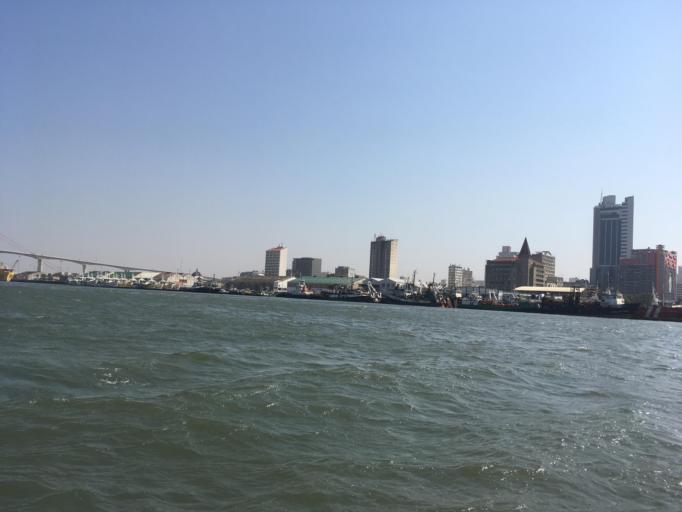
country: MZ
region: Maputo City
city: Maputo
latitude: -25.9789
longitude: 32.5686
